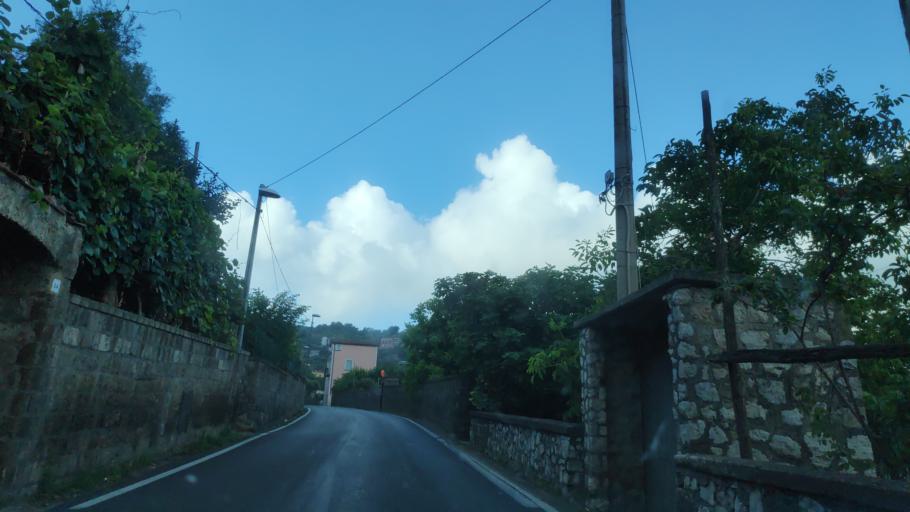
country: IT
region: Campania
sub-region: Provincia di Napoli
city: Piano di Sorrento
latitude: 40.6258
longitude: 14.4237
